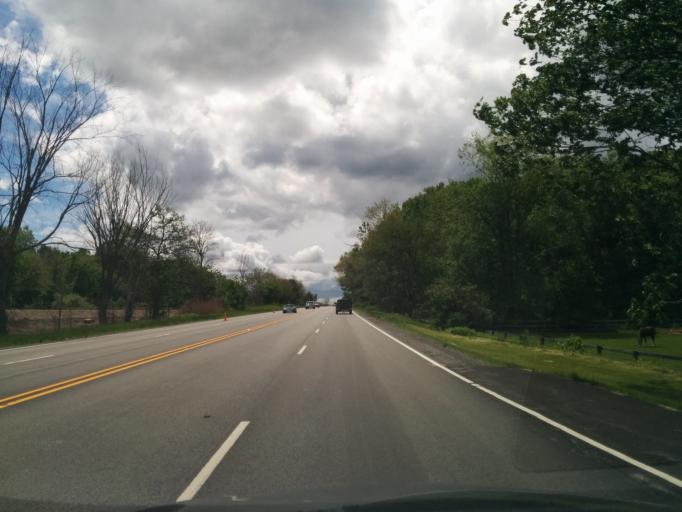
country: US
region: Indiana
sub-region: Porter County
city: Chesterton
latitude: 41.6510
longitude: -87.0095
